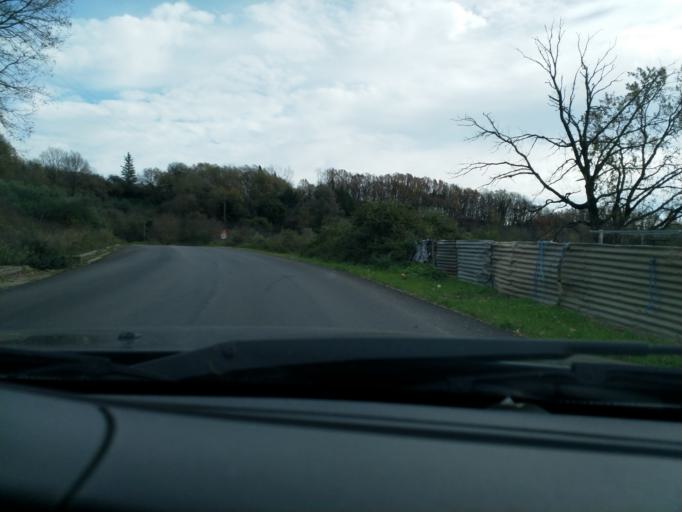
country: GR
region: Epirus
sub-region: Nomos Prevezis
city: Filippiada
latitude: 39.2175
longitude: 20.8579
